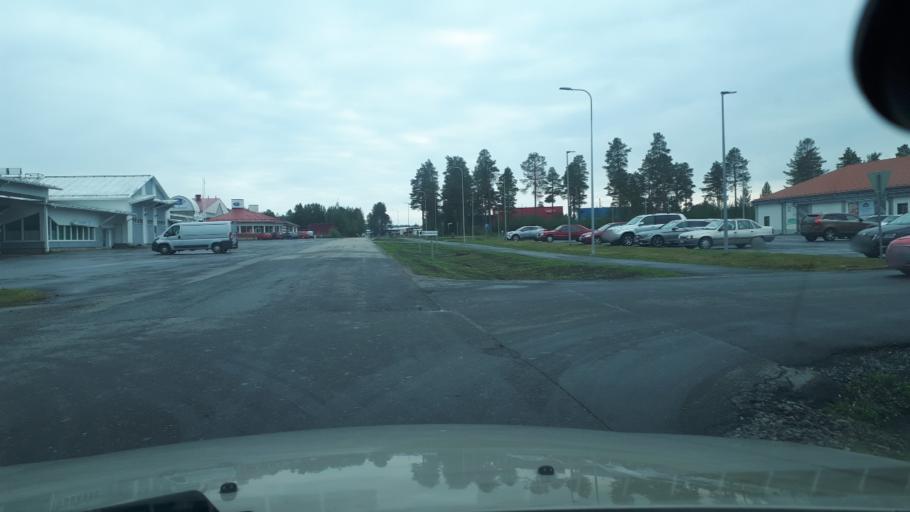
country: FI
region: Northern Ostrobothnia
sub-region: Oulu
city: Haukipudas
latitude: 65.1663
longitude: 25.3454
